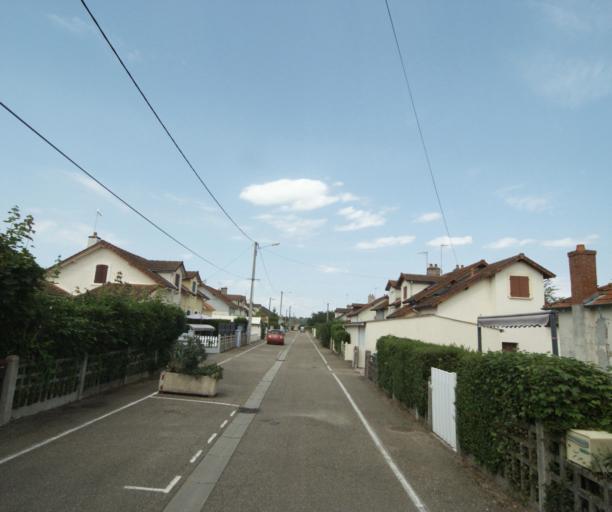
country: FR
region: Bourgogne
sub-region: Departement de Saone-et-Loire
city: Gueugnon
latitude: 46.6078
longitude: 4.0482
